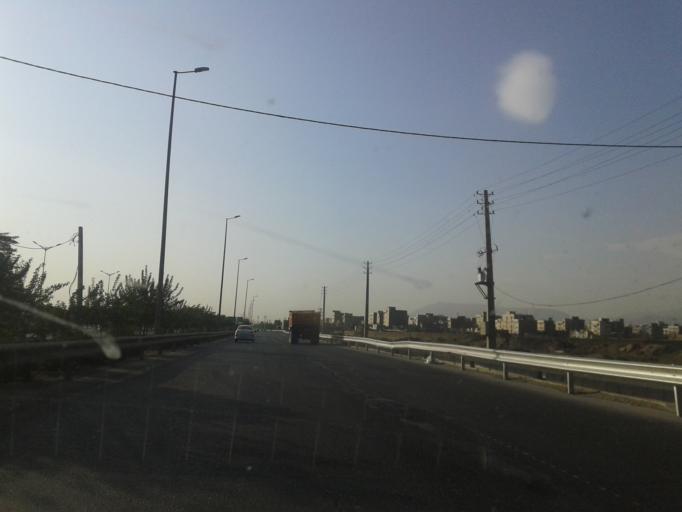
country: IR
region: Tehran
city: Eslamshahr
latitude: 35.6510
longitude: 51.2726
